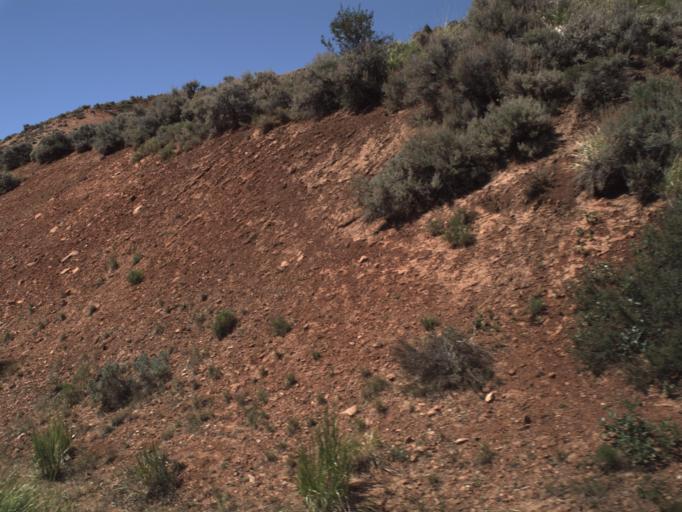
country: US
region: Utah
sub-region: Rich County
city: Randolph
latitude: 41.4812
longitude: -111.3719
